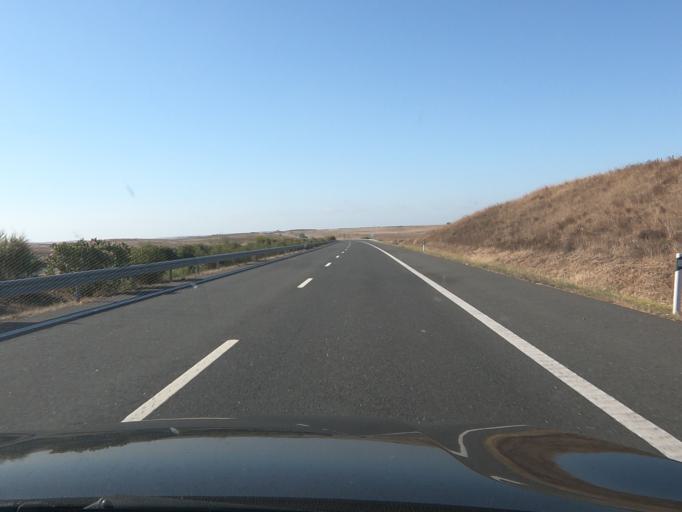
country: PT
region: Beja
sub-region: Aljustrel
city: Aljustrel
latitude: 37.8054
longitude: -8.2281
